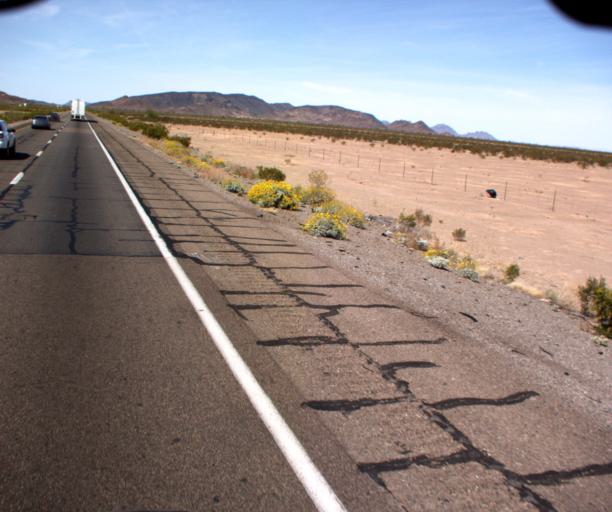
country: US
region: Arizona
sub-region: La Paz County
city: Salome
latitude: 33.6412
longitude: -113.8378
